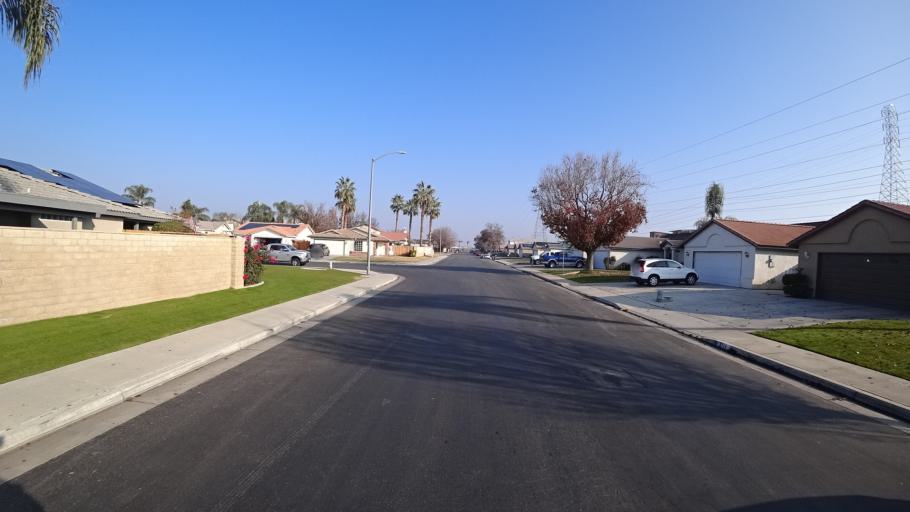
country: US
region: California
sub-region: Kern County
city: Greenacres
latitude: 35.3881
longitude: -119.0969
